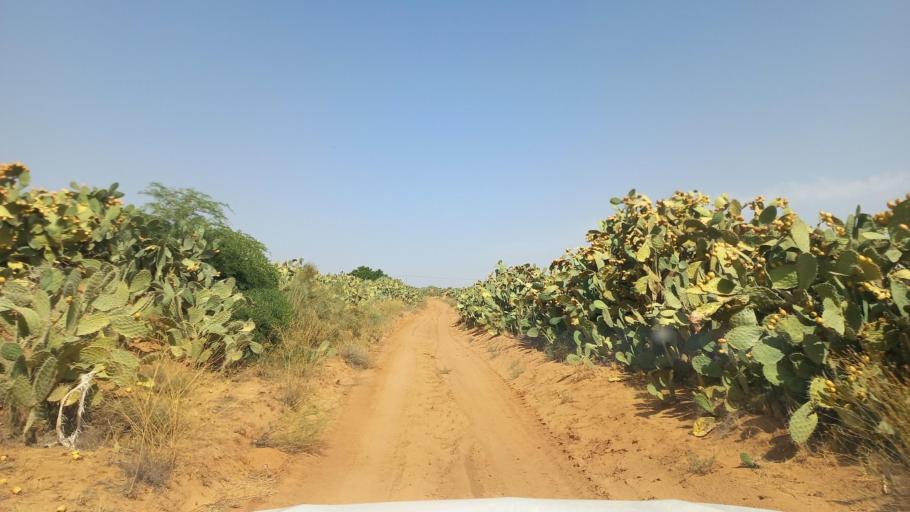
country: TN
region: Al Qasrayn
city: Kasserine
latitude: 35.2445
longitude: 9.0595
